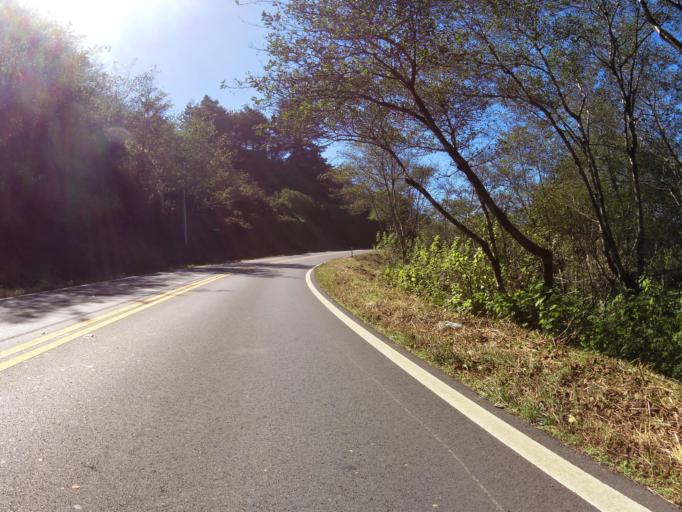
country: US
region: California
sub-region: Mendocino County
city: Fort Bragg
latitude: 39.6482
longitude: -123.7809
